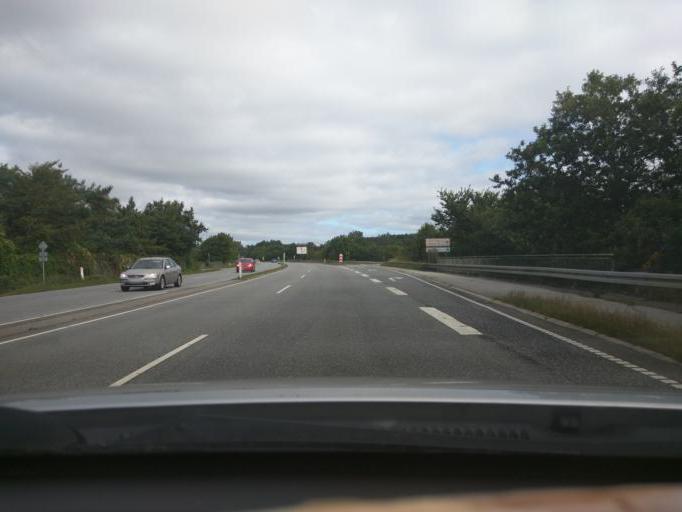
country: DK
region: Central Jutland
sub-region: Viborg Kommune
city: Viborg
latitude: 56.4290
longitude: 9.3901
